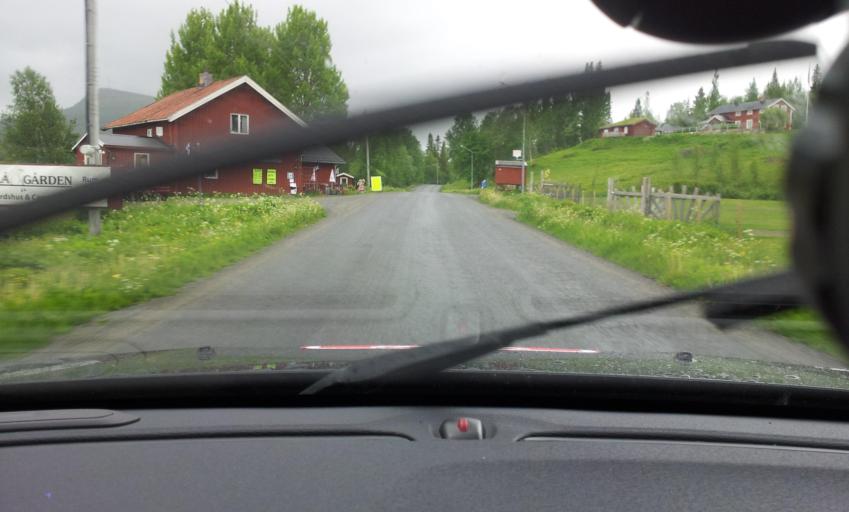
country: SE
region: Jaemtland
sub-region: Are Kommun
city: Are
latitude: 63.1664
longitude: 13.0602
